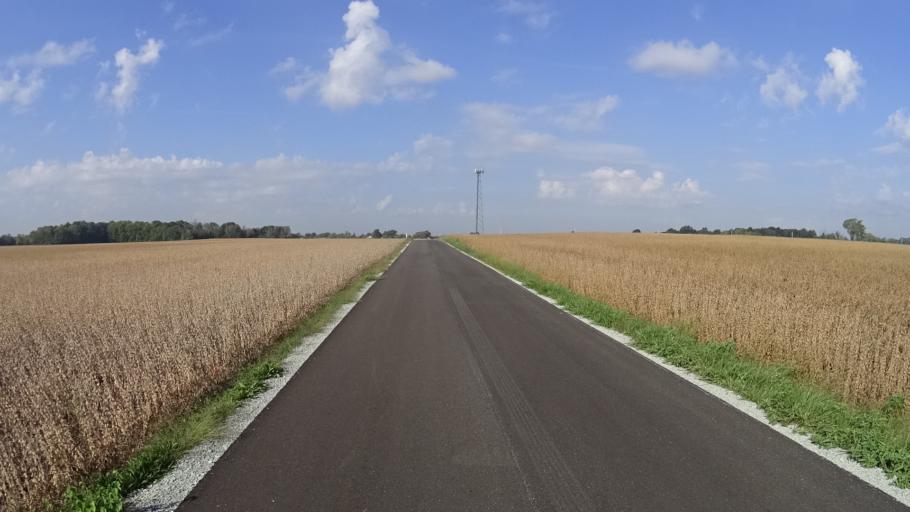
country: US
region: Indiana
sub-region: Madison County
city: Lapel
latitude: 40.0315
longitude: -85.8586
